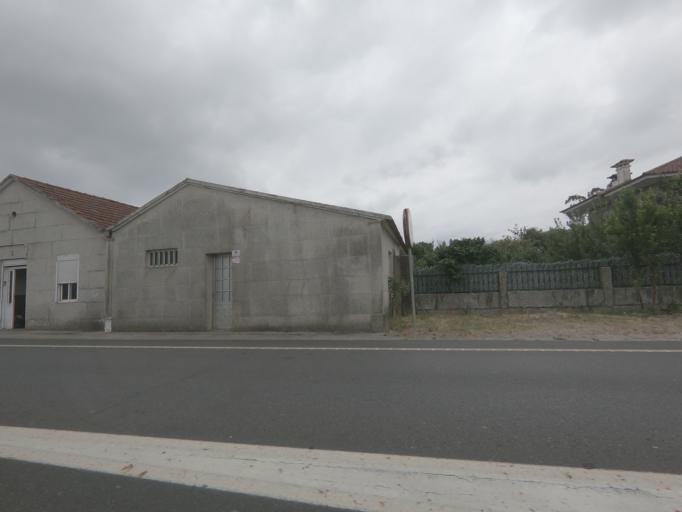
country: ES
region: Galicia
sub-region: Provincia de Pontevedra
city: Tomino
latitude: 41.9928
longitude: -8.7037
